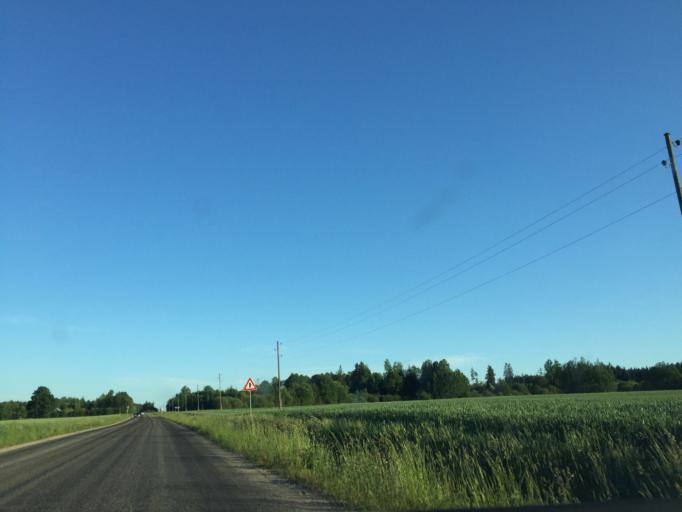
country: LV
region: Broceni
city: Broceni
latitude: 56.7176
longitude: 22.5008
